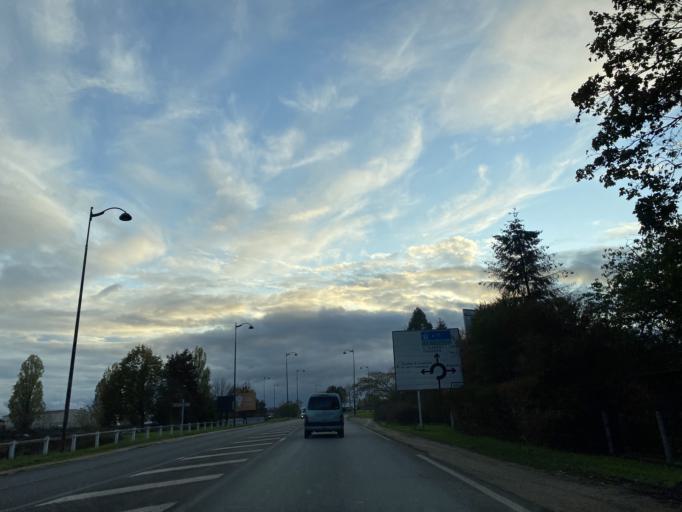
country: FR
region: Centre
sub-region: Departement du Cher
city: Bourges
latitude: 47.0630
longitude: 2.3667
